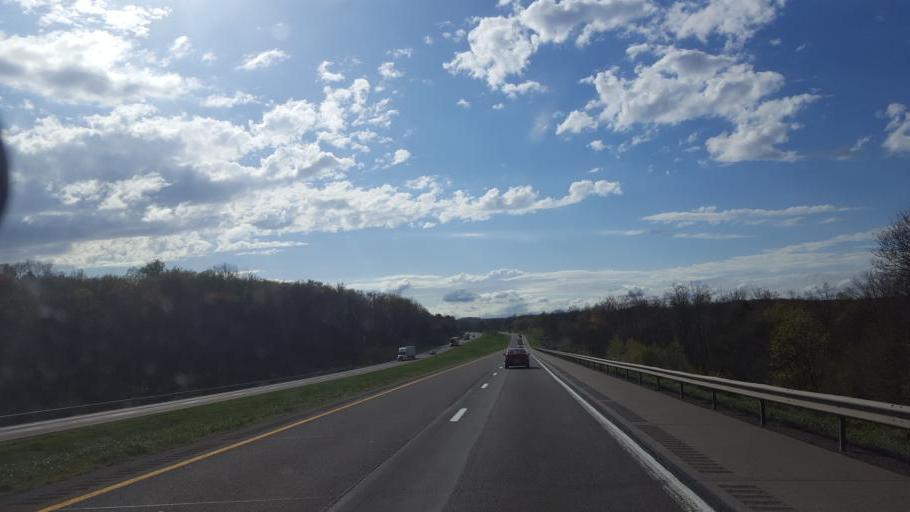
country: US
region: Pennsylvania
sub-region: Venango County
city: Seneca
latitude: 41.1806
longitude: -79.7667
